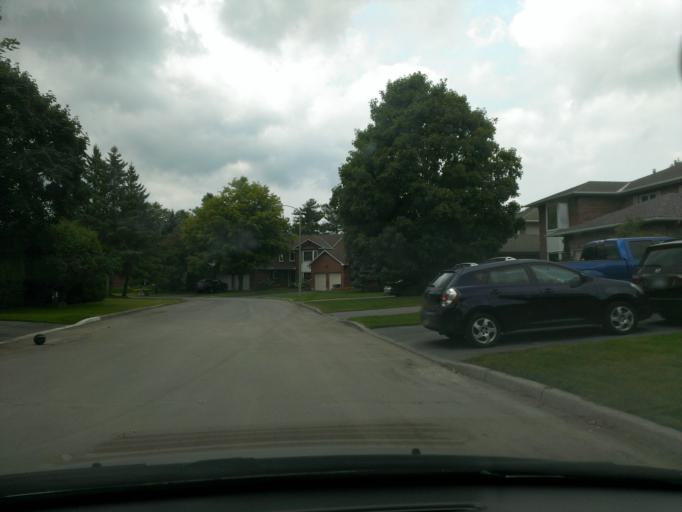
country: CA
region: Ontario
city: Clarence-Rockland
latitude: 45.4870
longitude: -75.4869
